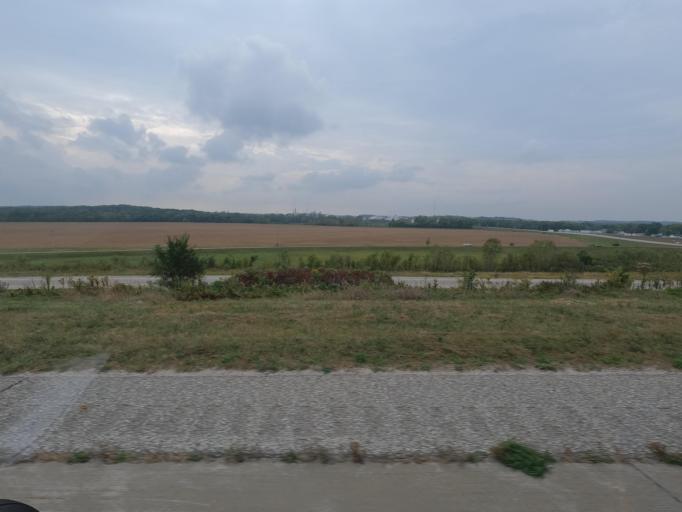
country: US
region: Iowa
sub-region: Wapello County
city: Eddyville
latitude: 41.1498
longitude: -92.6241
